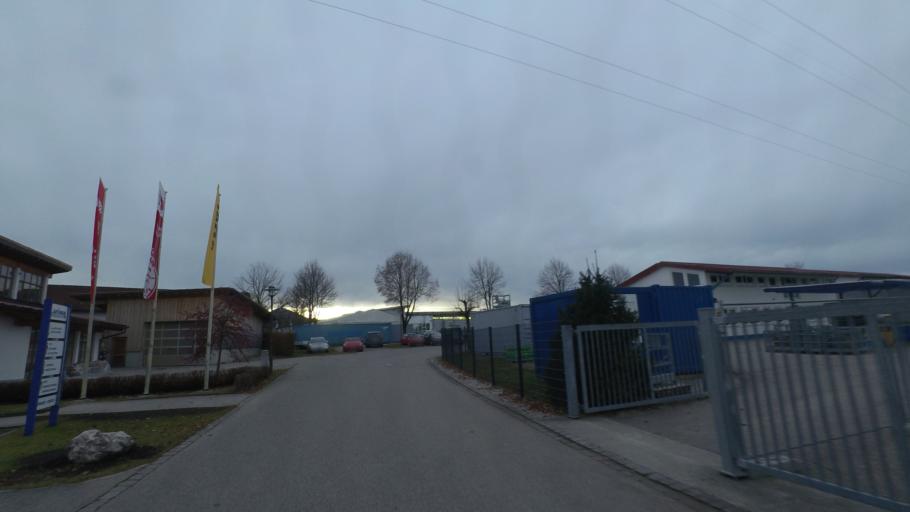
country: DE
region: Bavaria
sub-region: Upper Bavaria
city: Vachendorf
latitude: 47.8706
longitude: 12.6176
